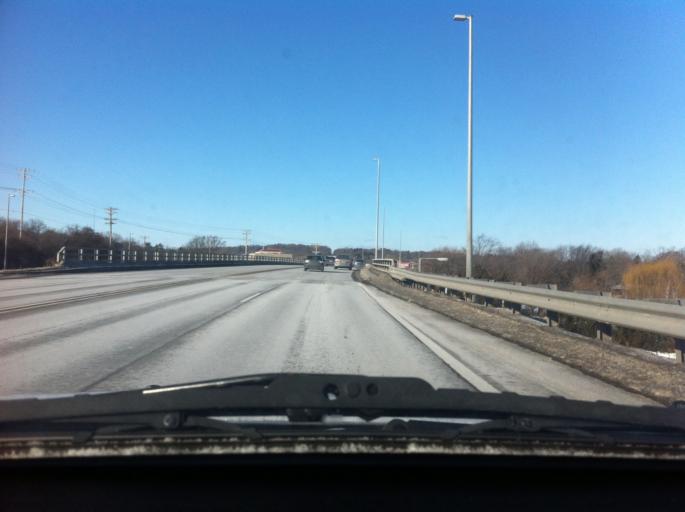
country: US
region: Wisconsin
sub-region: Dane County
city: Shorewood Hills
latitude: 43.0753
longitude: -89.4614
